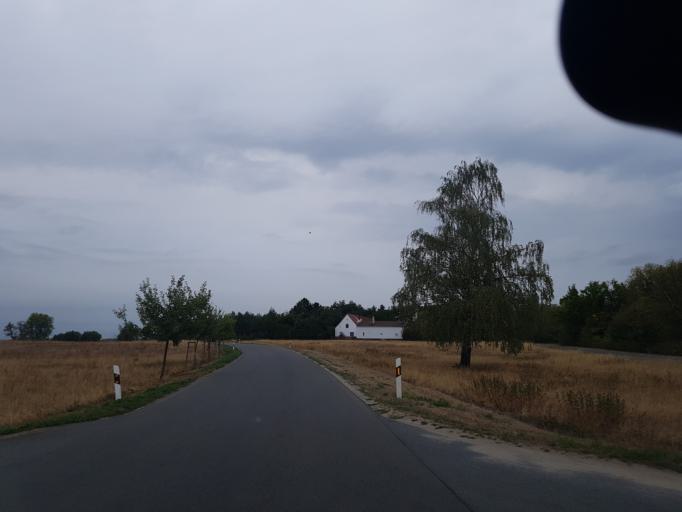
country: DE
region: Saxony-Anhalt
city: Prettin
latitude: 51.7094
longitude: 12.9004
